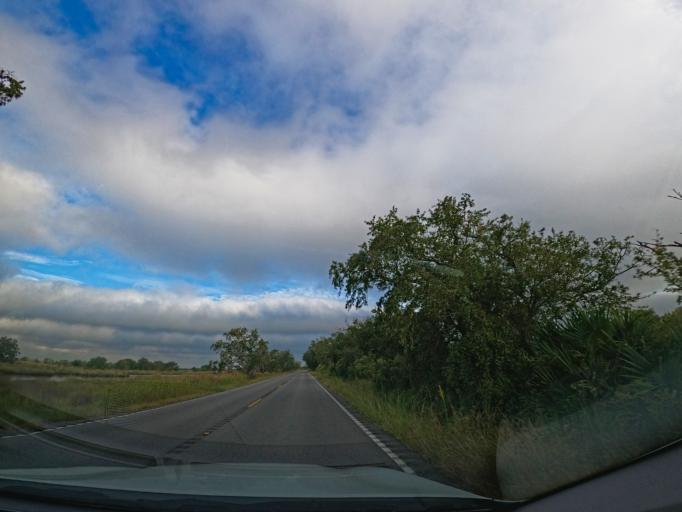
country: US
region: Louisiana
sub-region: Terrebonne Parish
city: Dulac
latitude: 29.3458
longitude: -90.6965
